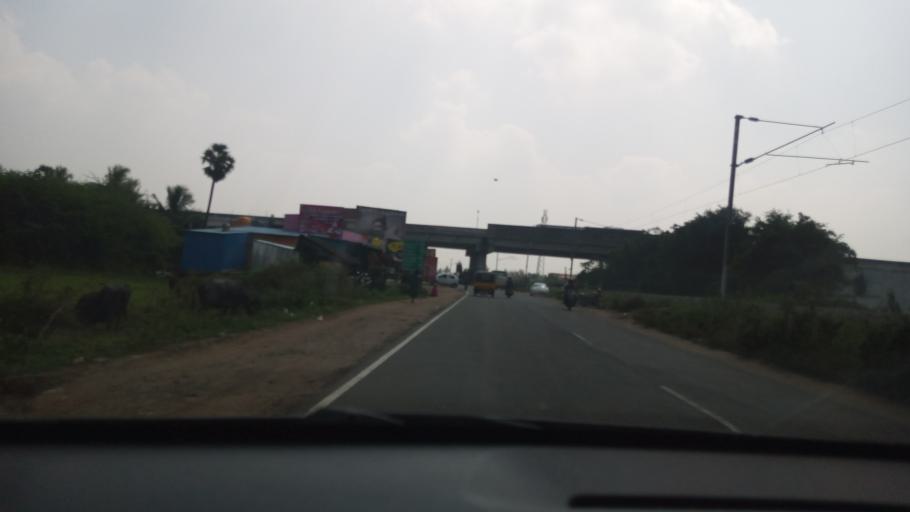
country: IN
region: Tamil Nadu
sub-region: Kancheepuram
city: Kanchipuram
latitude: 12.8755
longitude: 79.6903
